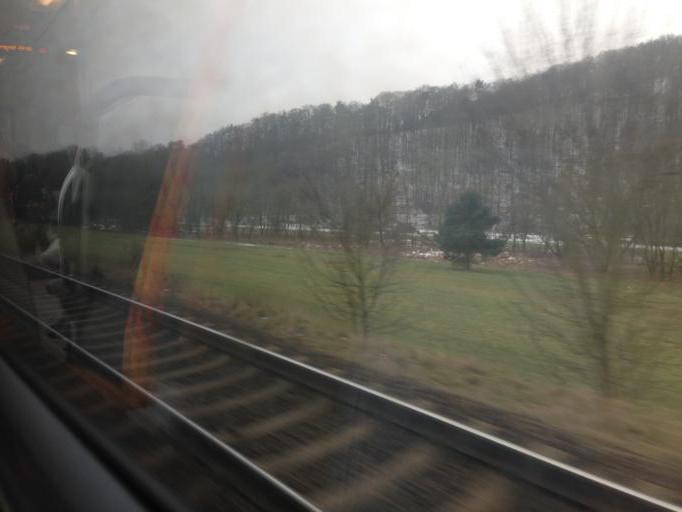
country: DE
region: Hesse
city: Herborn
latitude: 50.7049
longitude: 8.3055
